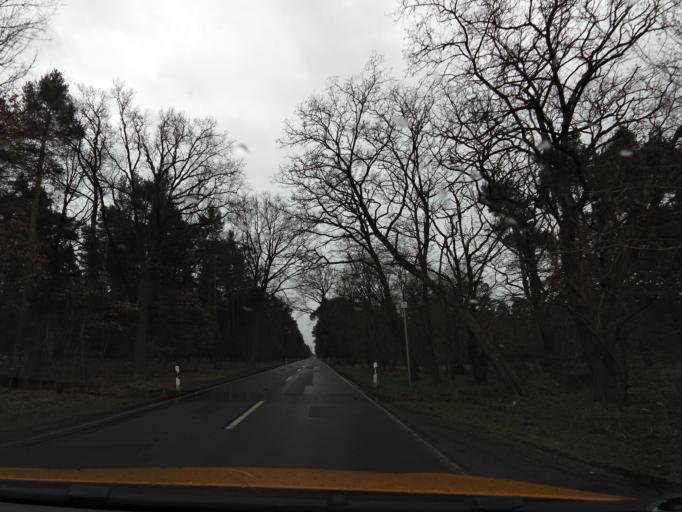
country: DE
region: Brandenburg
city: Ziesar
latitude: 52.3036
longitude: 12.3390
